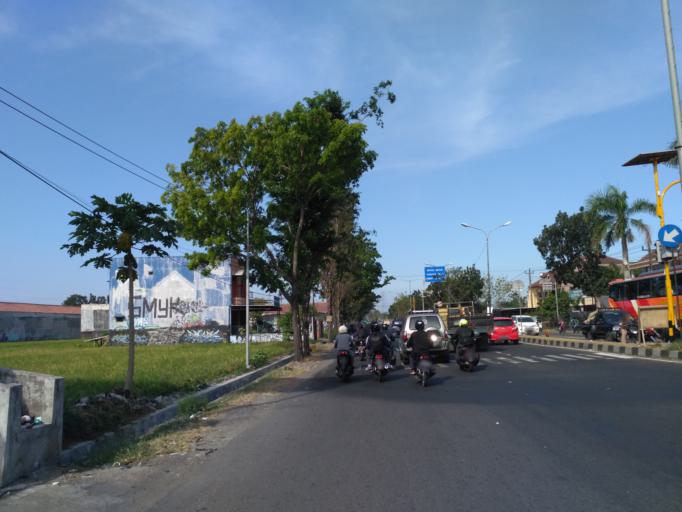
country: ID
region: Daerah Istimewa Yogyakarta
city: Kasihan
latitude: -7.8266
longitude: 110.3452
